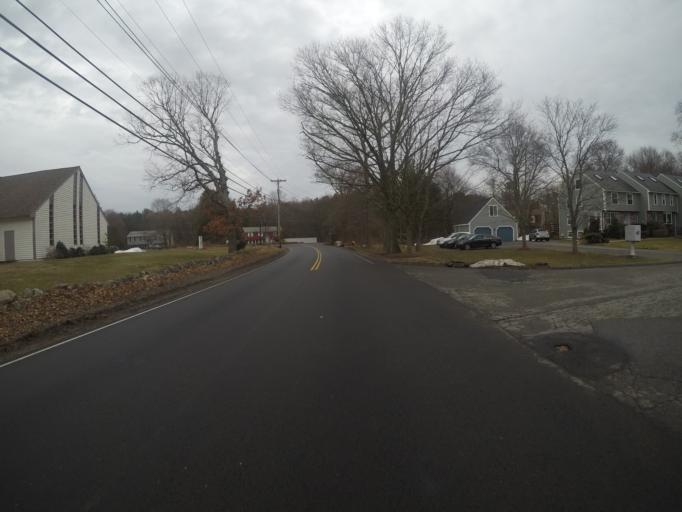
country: US
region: Massachusetts
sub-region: Bristol County
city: Easton
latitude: 42.0507
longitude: -71.1303
